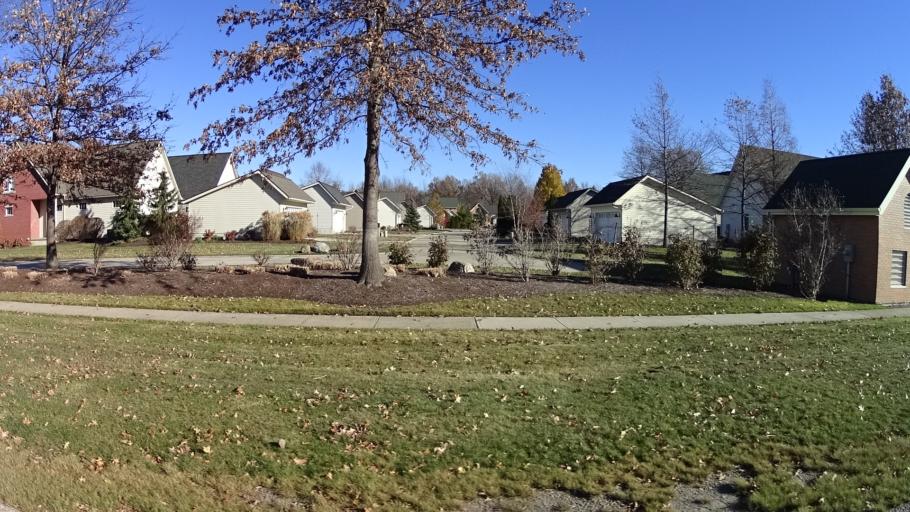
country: US
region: Ohio
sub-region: Lorain County
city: Avon Center
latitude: 41.4851
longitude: -81.9885
